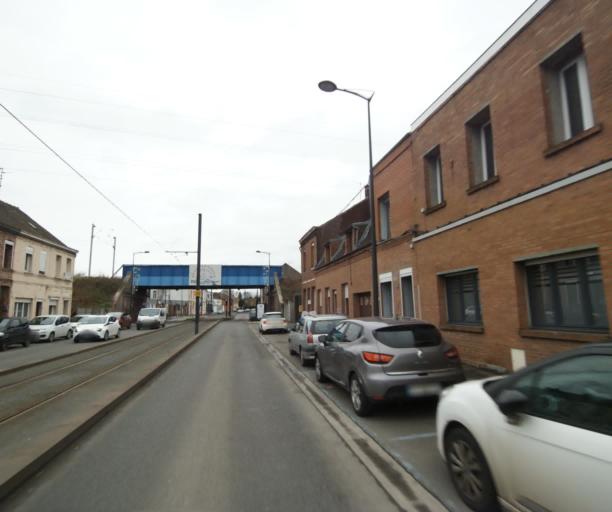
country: FR
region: Nord-Pas-de-Calais
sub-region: Departement du Nord
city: Bruay-sur-l'Escaut
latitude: 50.3874
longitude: 3.5264
